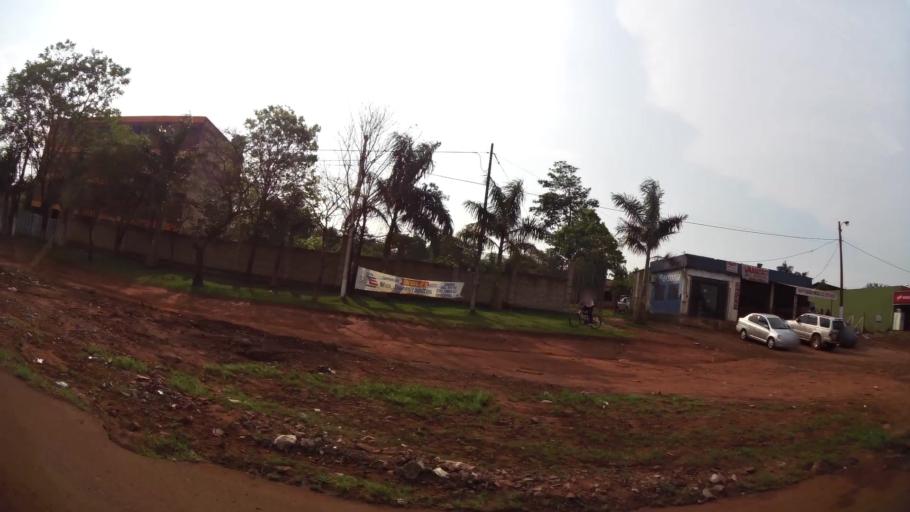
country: PY
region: Alto Parana
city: Ciudad del Este
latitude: -25.4879
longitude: -54.6628
